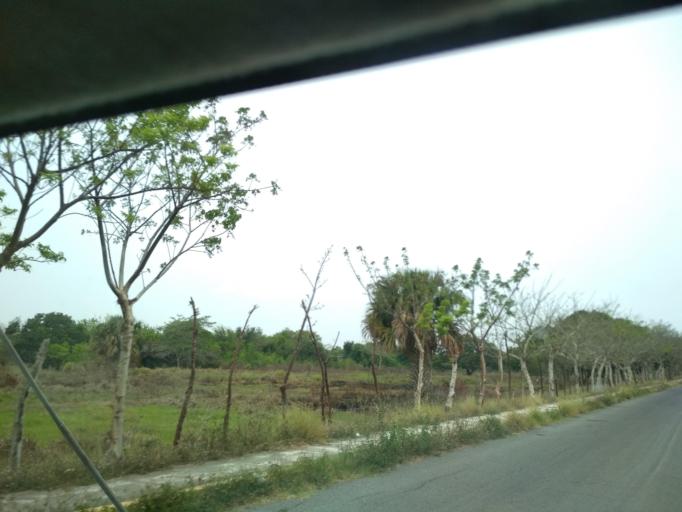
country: MX
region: Veracruz
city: Paso del Toro
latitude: 19.0466
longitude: -96.1496
